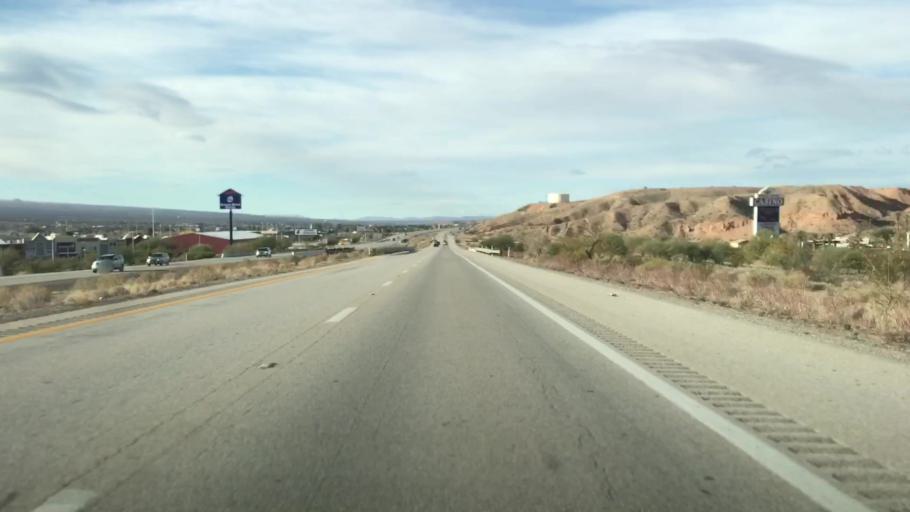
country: US
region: Nevada
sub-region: Clark County
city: Mesquite
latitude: 36.8136
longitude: -114.0629
